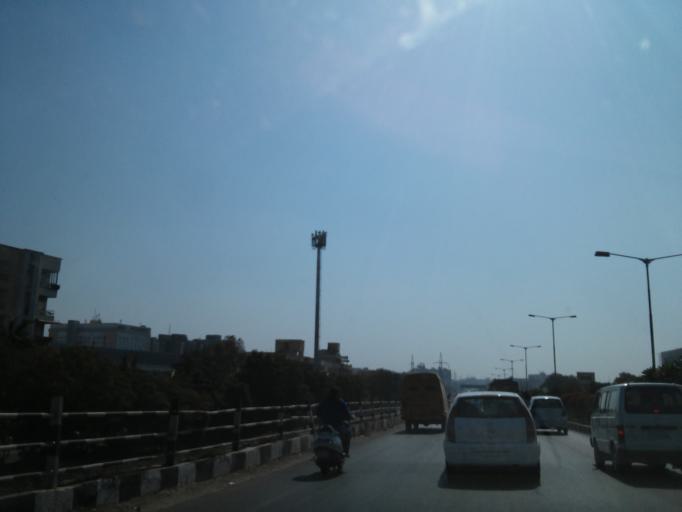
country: IN
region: Gujarat
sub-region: Ahmadabad
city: Ahmedabad
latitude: 23.0637
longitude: 72.5217
